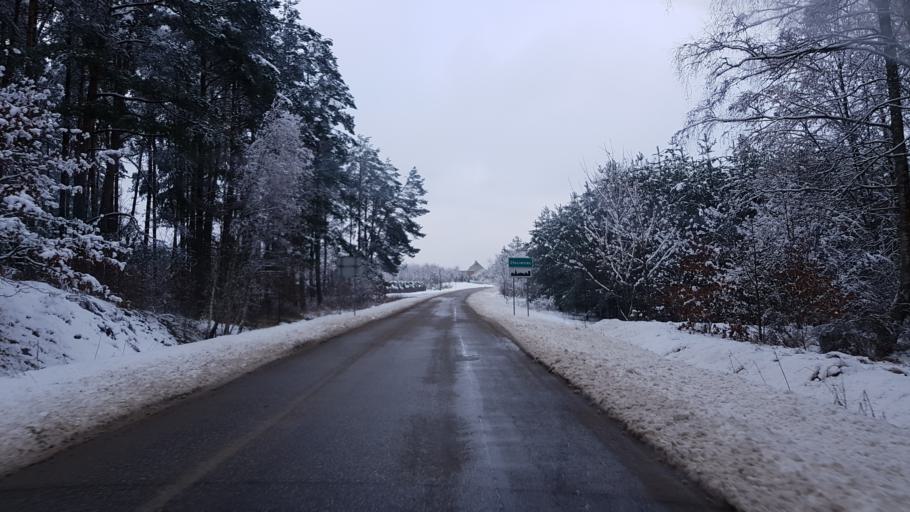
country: PL
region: West Pomeranian Voivodeship
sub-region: Powiat drawski
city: Zlocieniec
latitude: 53.5188
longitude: 16.0052
